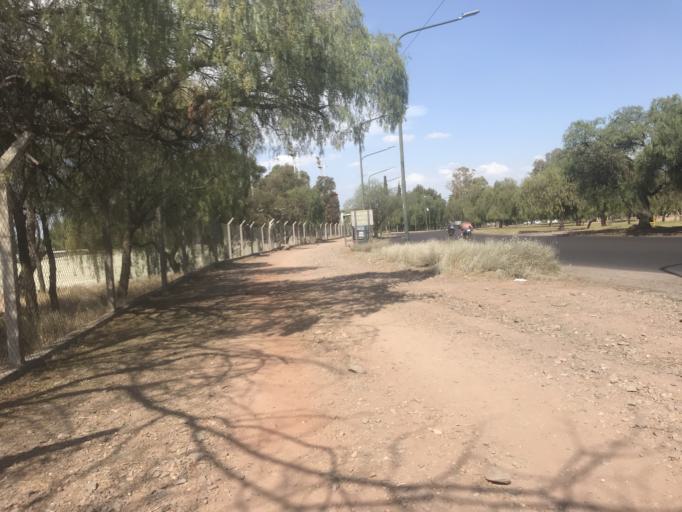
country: AR
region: Mendoza
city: Mendoza
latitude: -32.8819
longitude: -68.8839
